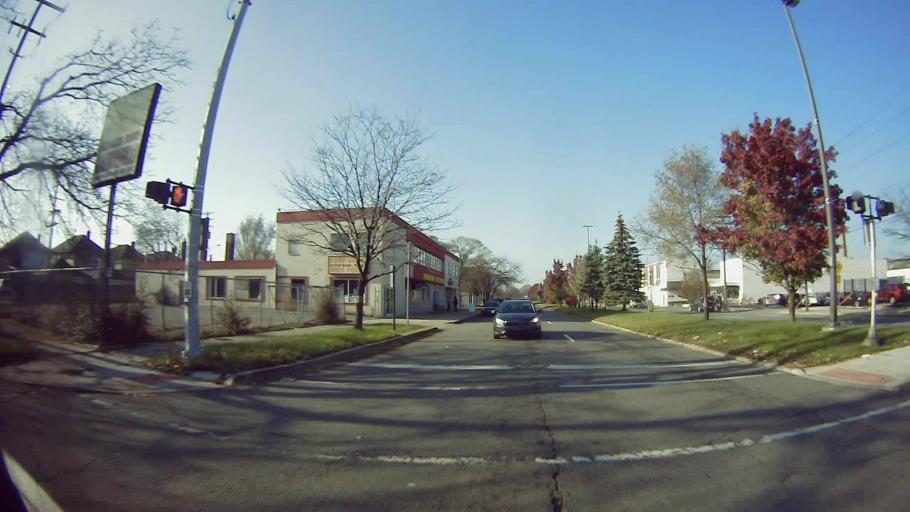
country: US
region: Michigan
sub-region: Wayne County
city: Highland Park
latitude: 42.4006
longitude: -83.1185
